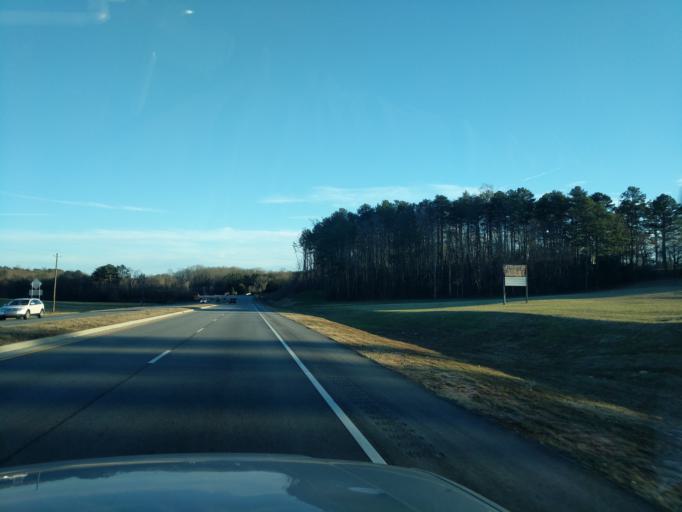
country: US
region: Georgia
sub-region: Stephens County
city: Toccoa
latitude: 34.5399
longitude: -83.2670
